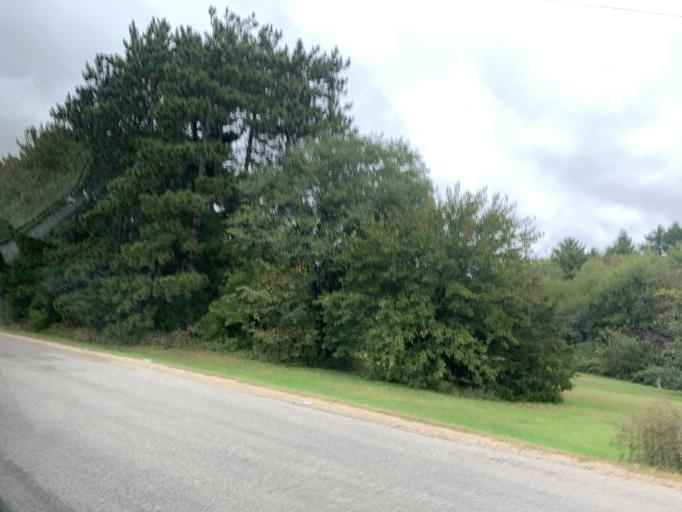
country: US
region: Wisconsin
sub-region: Sauk County
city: Prairie du Sac
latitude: 43.2931
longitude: -89.7788
